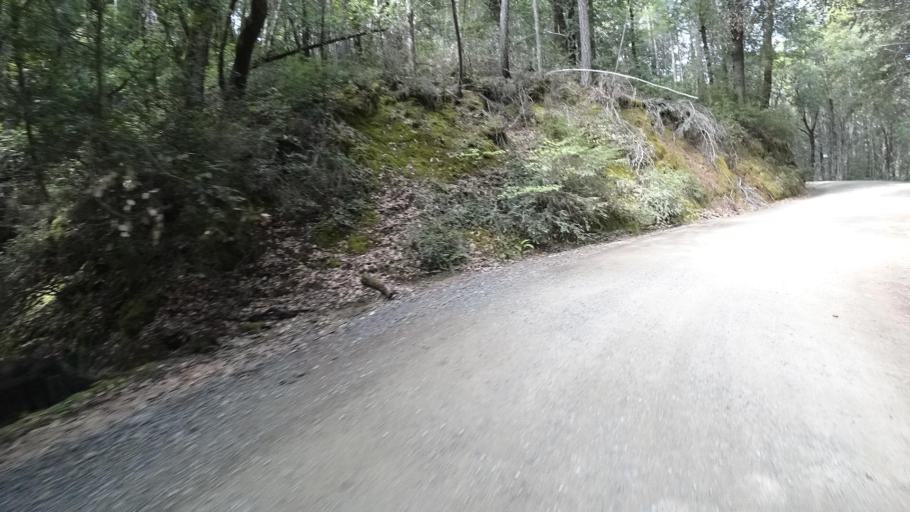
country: US
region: California
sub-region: Humboldt County
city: Redway
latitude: 40.0301
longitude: -123.8350
